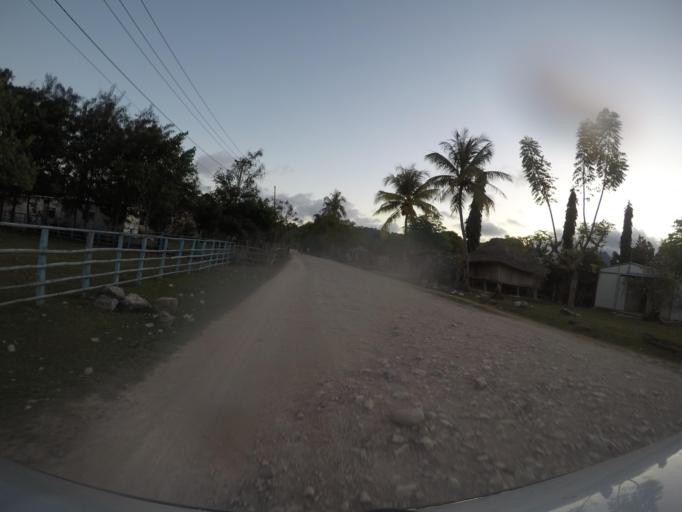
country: TL
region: Viqueque
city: Viqueque
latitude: -8.7751
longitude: 126.6379
